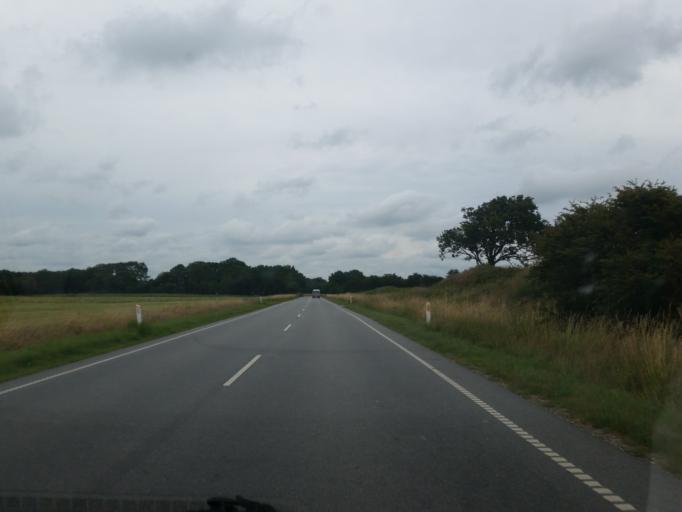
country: DK
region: South Denmark
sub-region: Vejen Kommune
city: Holsted
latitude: 55.4095
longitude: 8.9400
